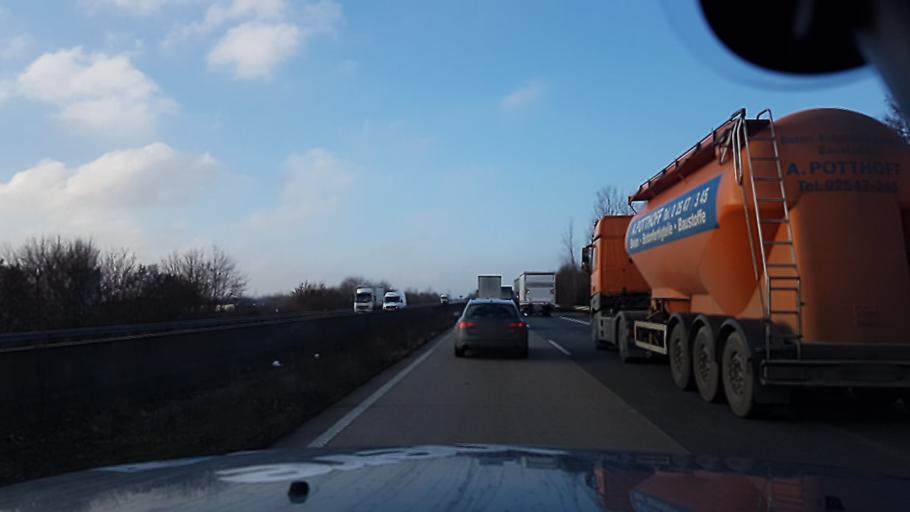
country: DE
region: North Rhine-Westphalia
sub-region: Regierungsbezirk Munster
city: Dreierwalde
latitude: 52.3135
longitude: 7.4640
